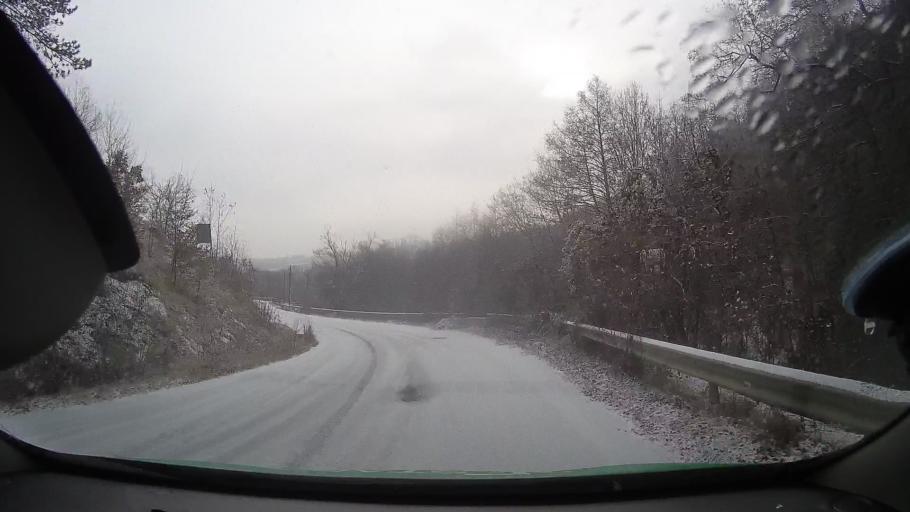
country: RO
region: Alba
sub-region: Comuna Livezile
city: Livezile
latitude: 46.3696
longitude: 23.5883
